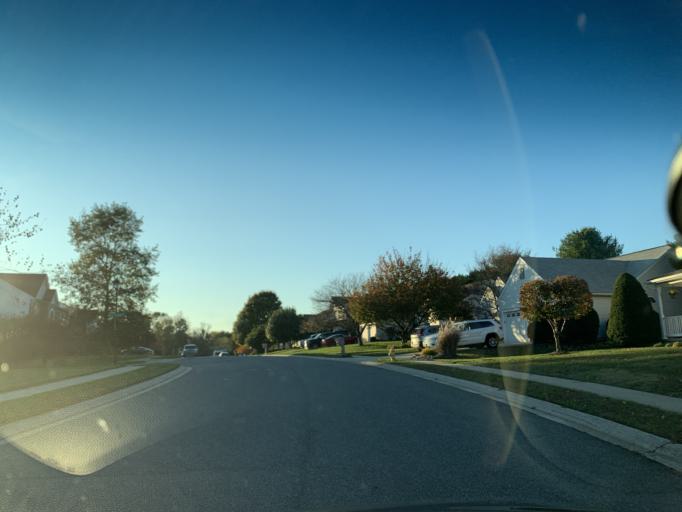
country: US
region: Maryland
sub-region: Harford County
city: Bel Air North
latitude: 39.5641
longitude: -76.3810
